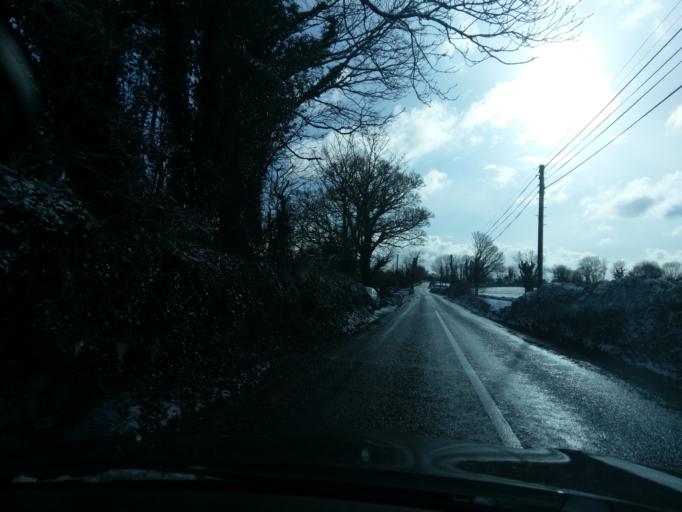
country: IE
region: Connaught
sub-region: County Galway
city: Athenry
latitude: 53.2249
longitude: -8.7391
